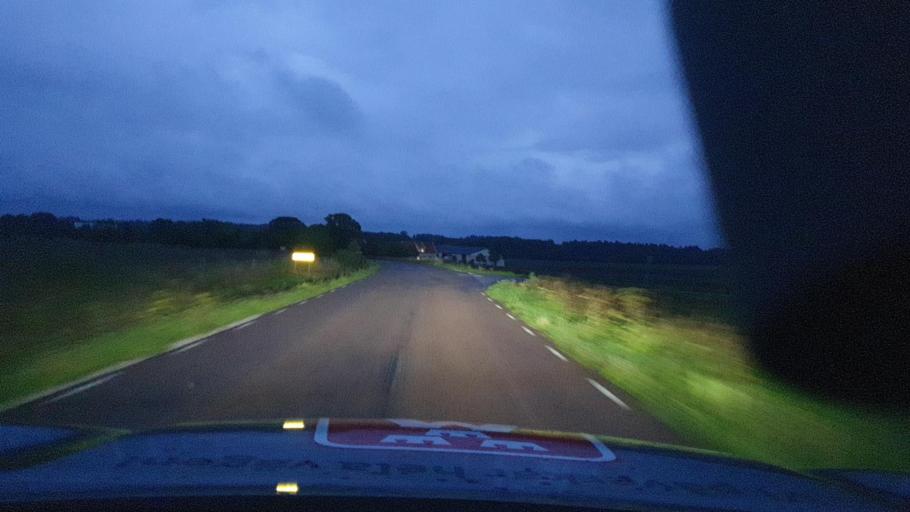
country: SE
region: Gotland
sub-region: Gotland
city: Slite
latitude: 57.7601
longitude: 18.8768
